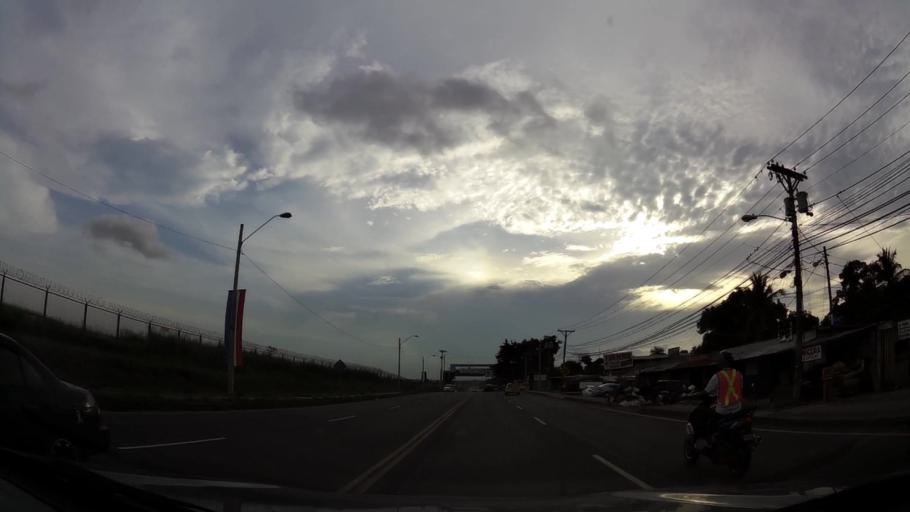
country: PA
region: Panama
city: Tocumen
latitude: 9.0927
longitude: -79.3782
